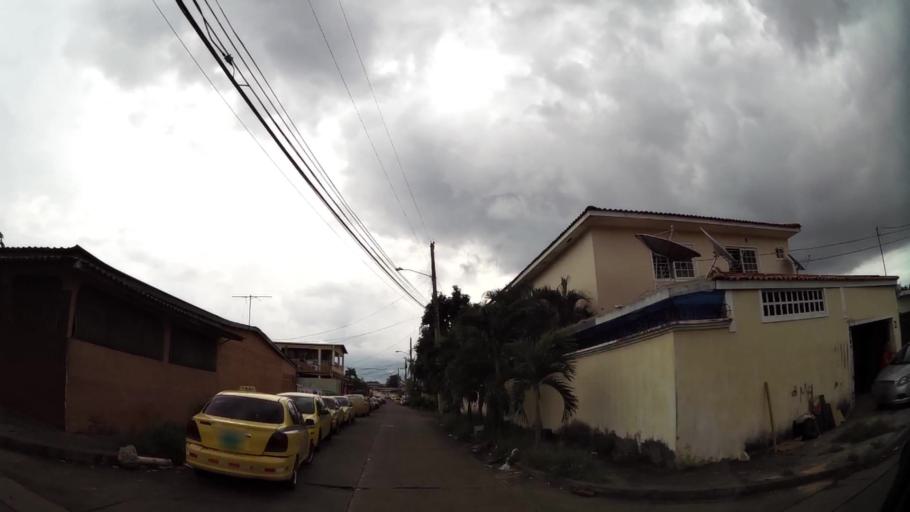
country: PA
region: Panama
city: Tocumen
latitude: 9.0595
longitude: -79.4152
